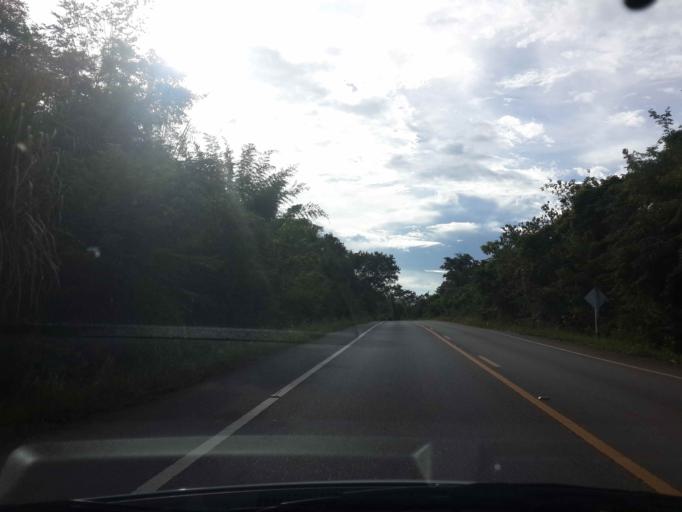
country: TH
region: Kanchanaburi
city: Sai Yok
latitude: 13.9276
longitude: 99.1211
